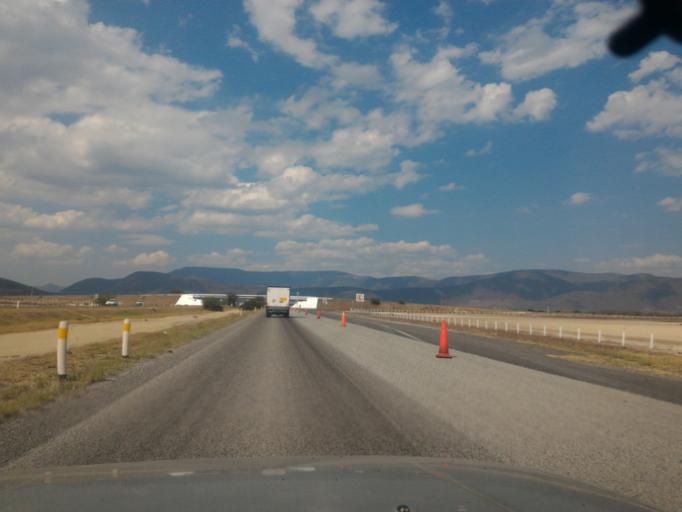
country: MX
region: Jalisco
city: Atoyac
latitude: 20.1266
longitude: -103.5080
